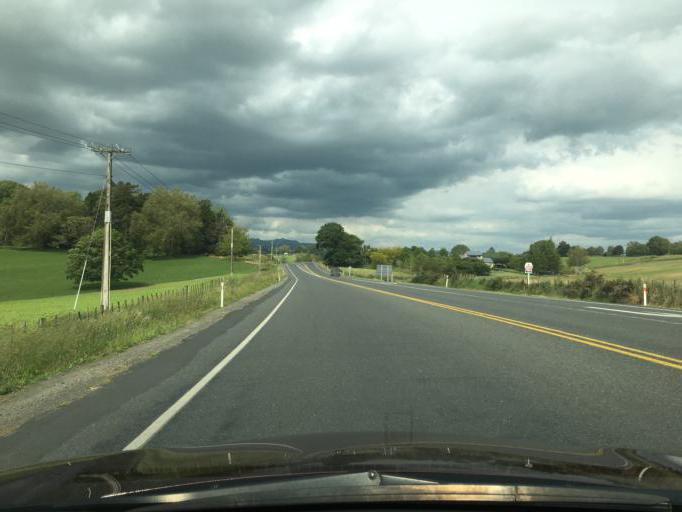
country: NZ
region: Waikato
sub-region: Waipa District
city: Cambridge
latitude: -38.0152
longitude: 175.3589
